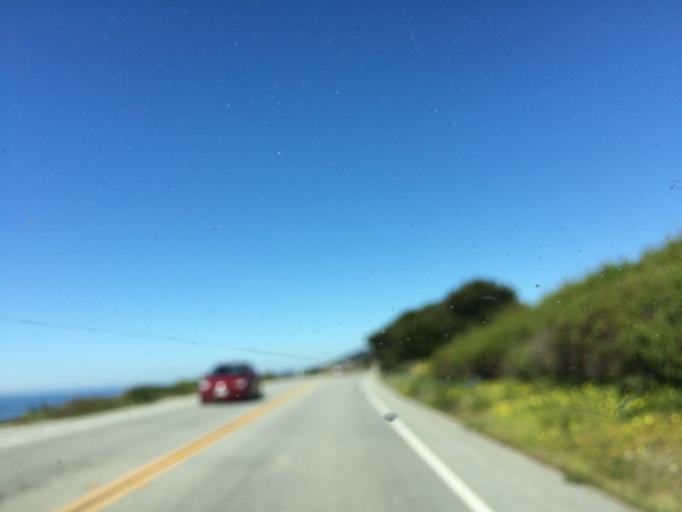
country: US
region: California
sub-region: Santa Cruz County
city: Bonny Doon
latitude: 37.0619
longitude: -122.2518
